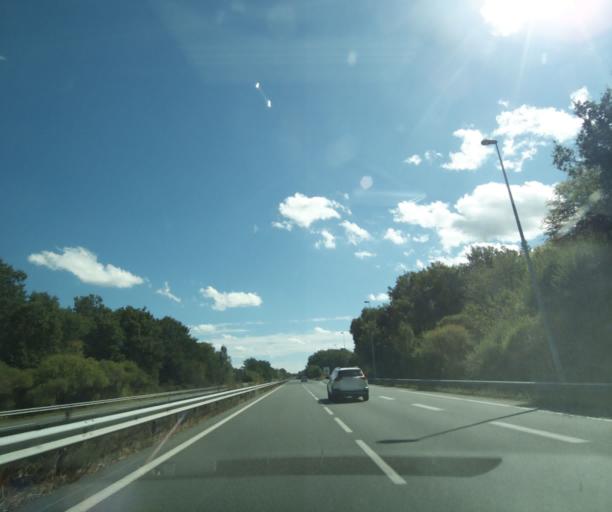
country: FR
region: Aquitaine
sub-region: Departement du Lot-et-Garonne
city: Fourques-sur-Garonne
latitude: 44.4082
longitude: 0.1832
